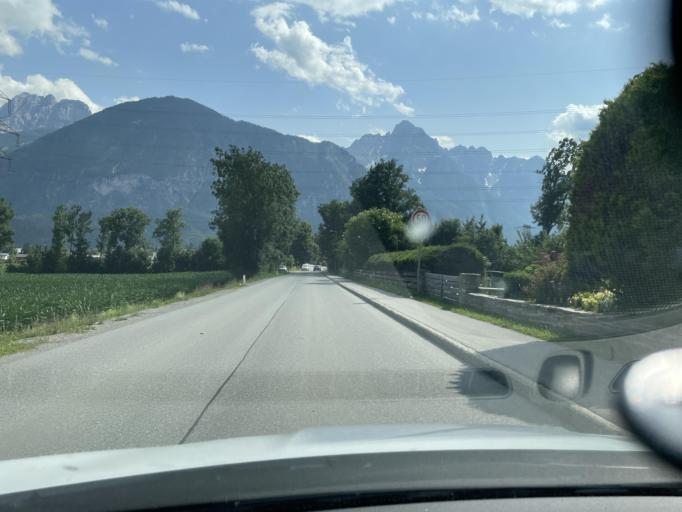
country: AT
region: Tyrol
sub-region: Politischer Bezirk Lienz
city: Lienz
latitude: 46.8381
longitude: 12.7777
